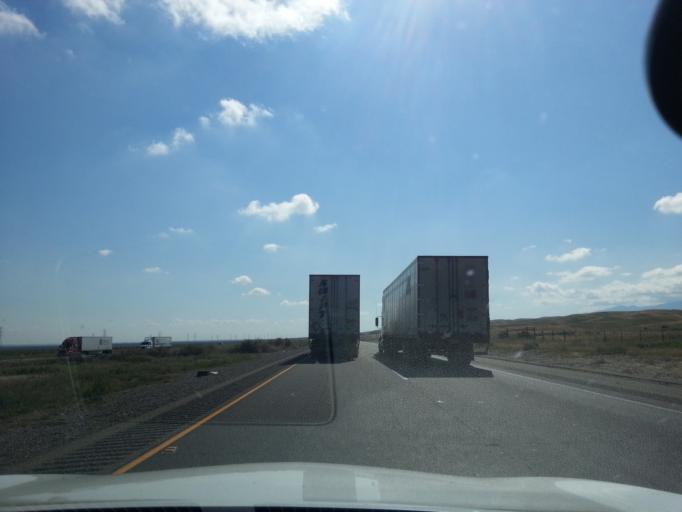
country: US
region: California
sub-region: Fresno County
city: Mendota
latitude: 36.5065
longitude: -120.4604
